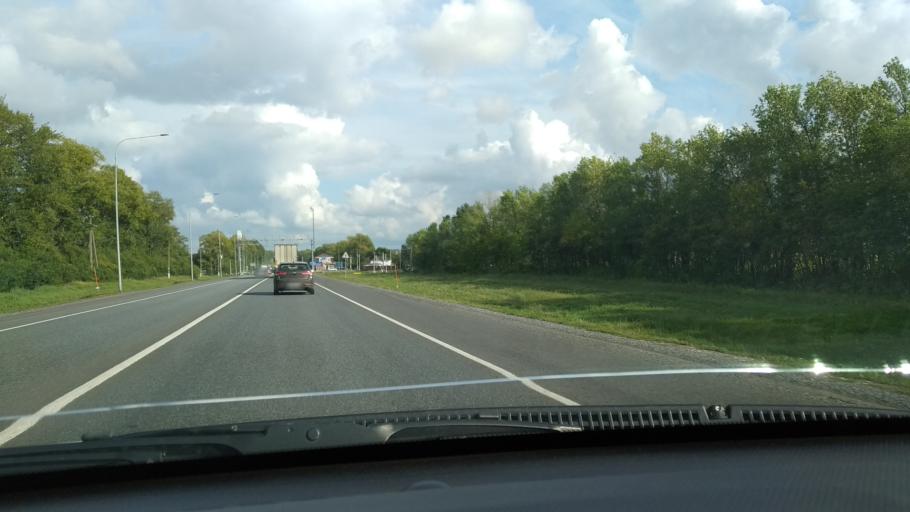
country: RU
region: Tatarstan
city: Stolbishchi
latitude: 55.6573
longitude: 49.3080
